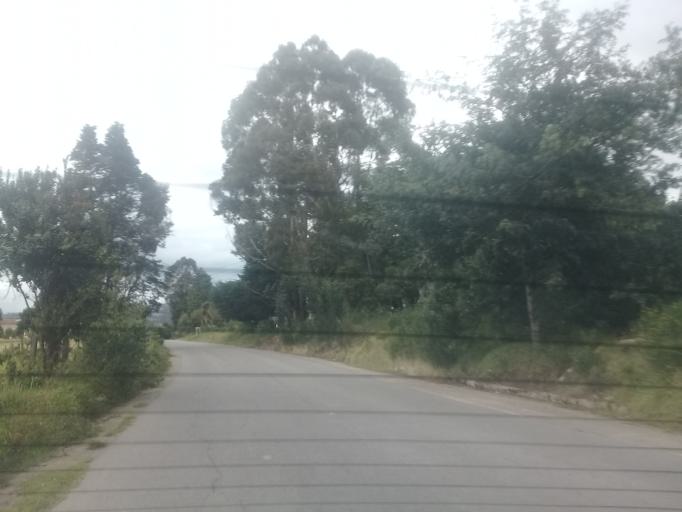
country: CO
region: Cundinamarca
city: Subachoque
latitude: 4.9290
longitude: -74.1520
